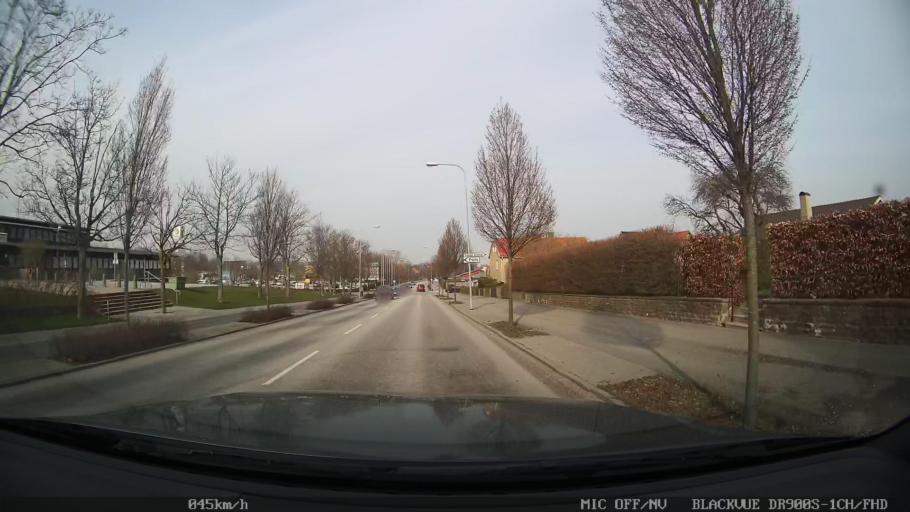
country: SE
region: Skane
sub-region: Ystads Kommun
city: Ystad
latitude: 55.4390
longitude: 13.8276
